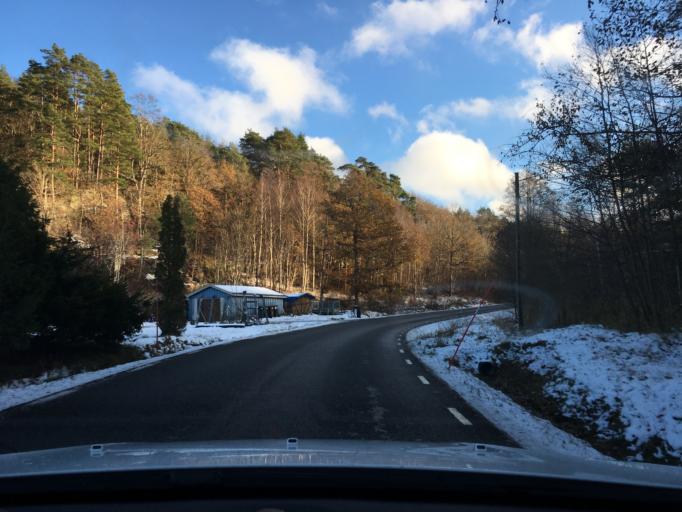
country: SE
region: Vaestra Goetaland
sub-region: Tjorns Kommun
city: Myggenas
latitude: 58.0587
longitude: 11.6913
